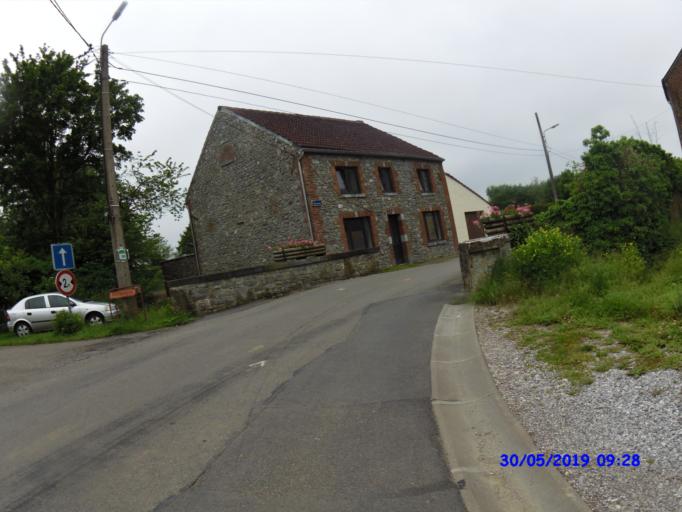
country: BE
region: Wallonia
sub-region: Province du Hainaut
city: Beaumont
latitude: 50.2598
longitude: 4.3148
